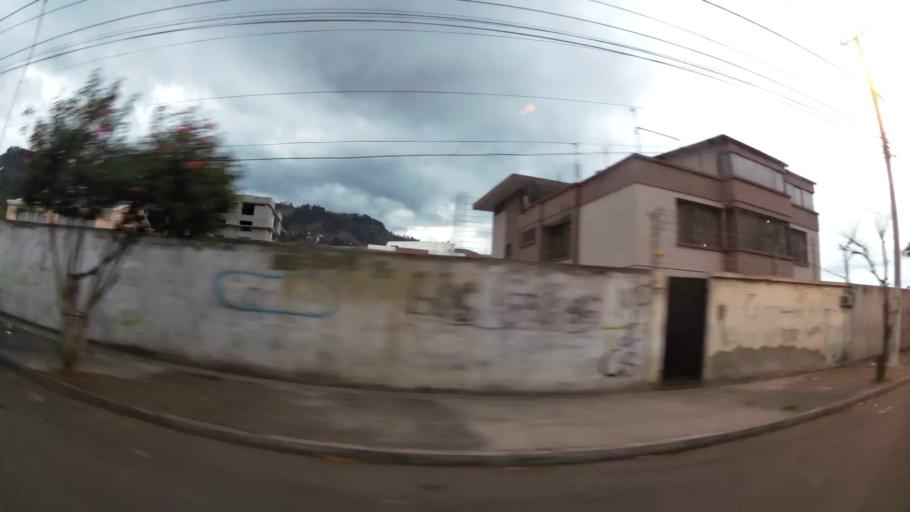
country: EC
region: Tungurahua
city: Ambato
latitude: -1.2508
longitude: -78.6390
